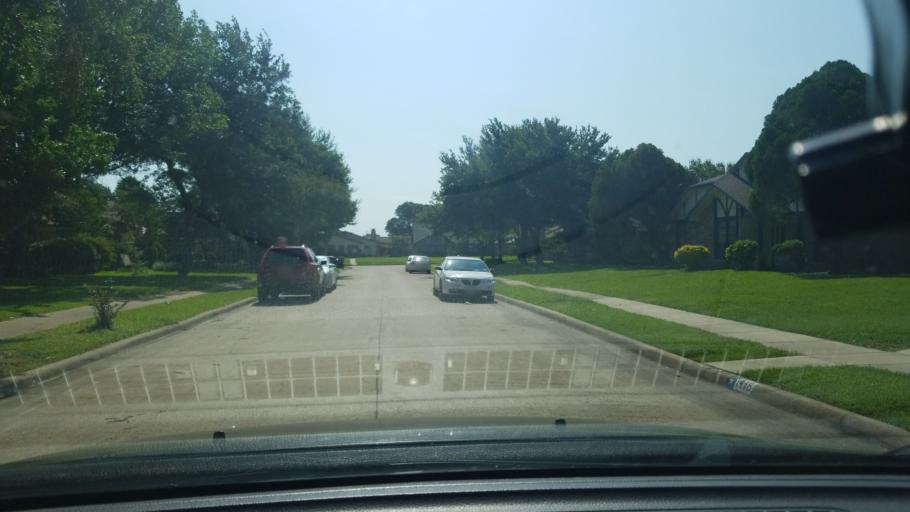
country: US
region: Texas
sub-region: Dallas County
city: Mesquite
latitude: 32.8183
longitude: -96.6192
